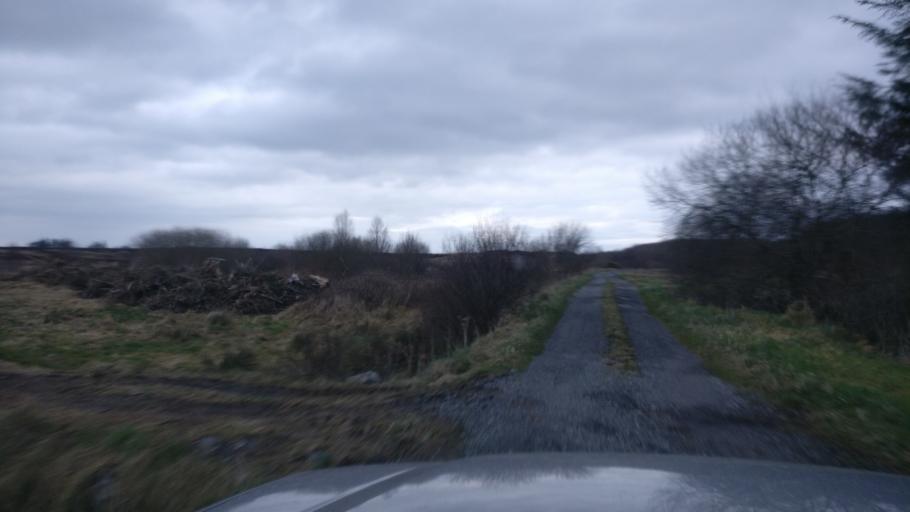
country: IE
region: Connaught
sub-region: County Galway
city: Loughrea
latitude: 53.2728
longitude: -8.4617
